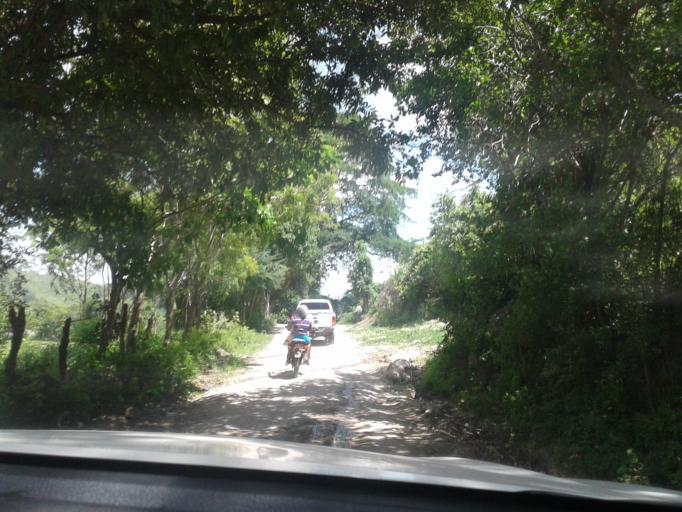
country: NI
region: Matagalpa
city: Terrabona
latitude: 12.5570
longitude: -86.0334
